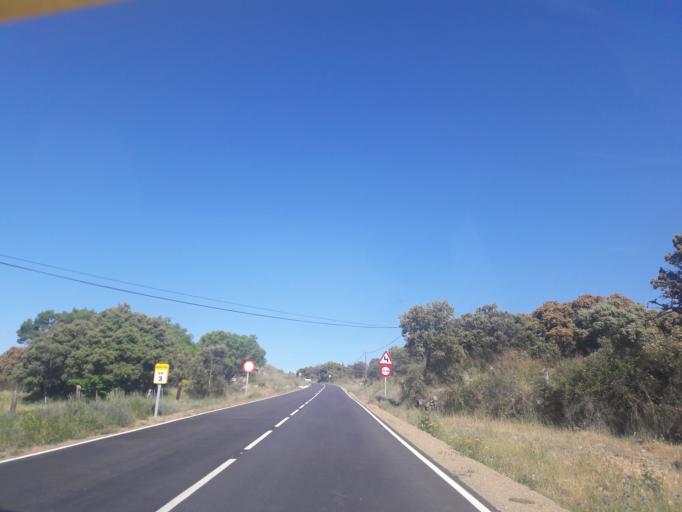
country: ES
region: Castille and Leon
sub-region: Provincia de Salamanca
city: Nava de Bejar
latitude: 40.4841
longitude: -5.6486
